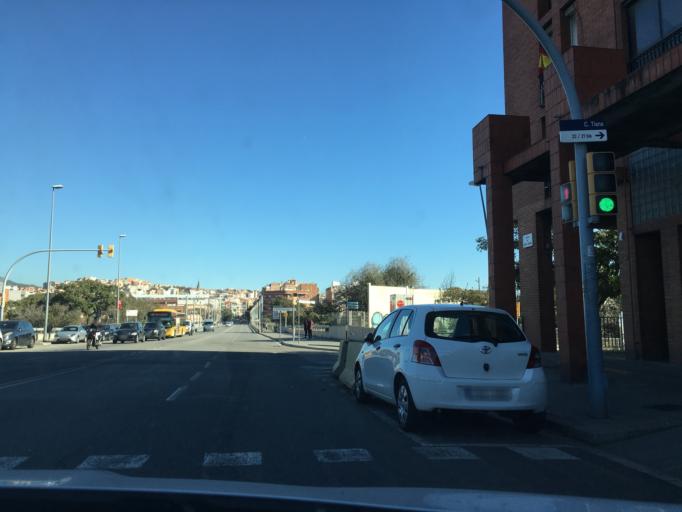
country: ES
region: Catalonia
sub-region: Provincia de Barcelona
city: Santa Coloma de Gramenet
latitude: 41.4485
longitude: 2.1999
